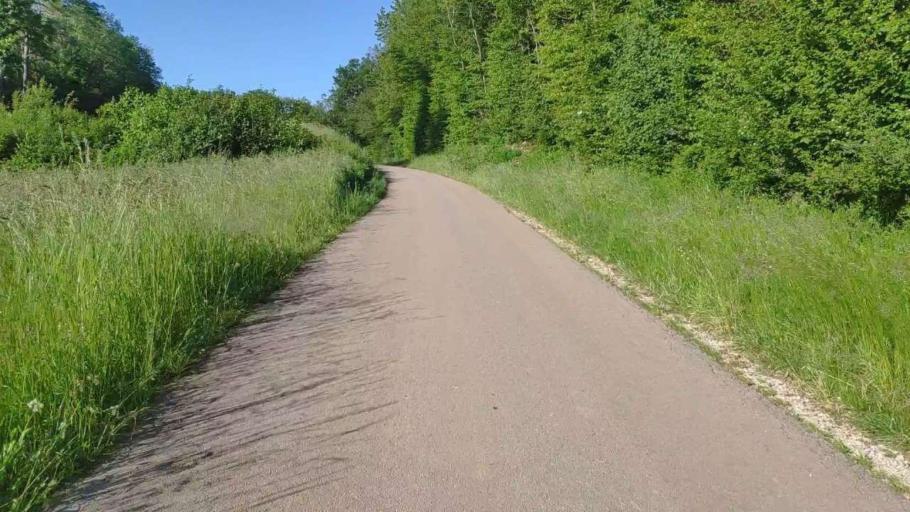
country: FR
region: Franche-Comte
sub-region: Departement du Jura
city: Perrigny
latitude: 46.7228
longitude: 5.6113
